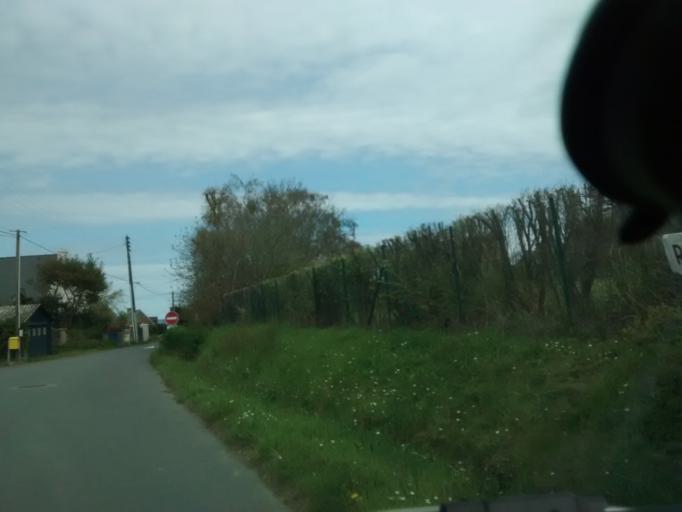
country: FR
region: Brittany
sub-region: Departement des Cotes-d'Armor
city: Ploubazlanec
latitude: 48.8079
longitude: -3.0178
